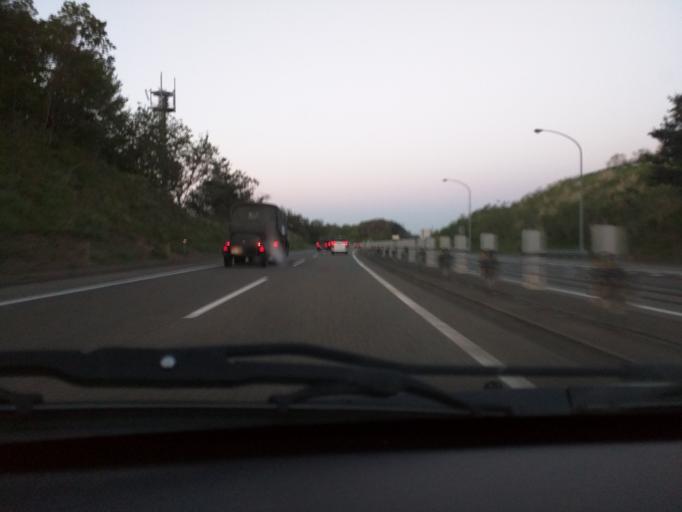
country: JP
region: Niigata
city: Kashiwazaki
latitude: 37.3479
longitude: 138.4979
